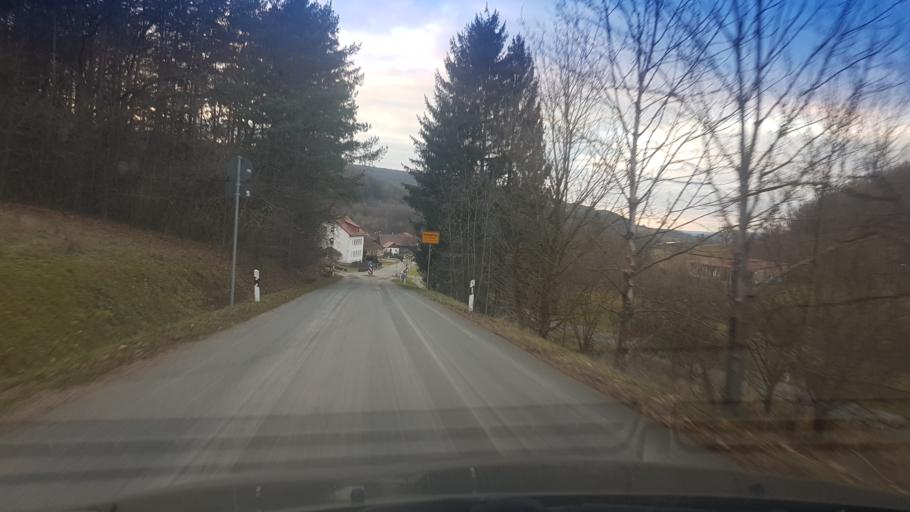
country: DE
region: Bavaria
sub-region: Upper Franconia
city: Wattendorf
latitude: 50.0652
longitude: 11.0790
